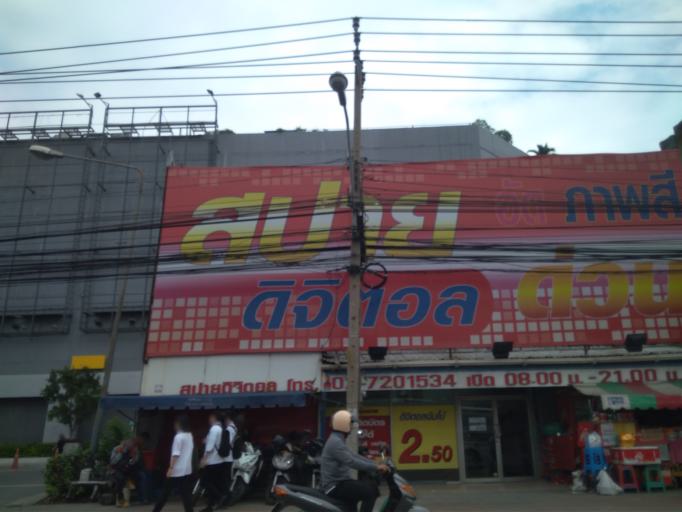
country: TH
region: Bangkok
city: Bang Na
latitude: 13.6923
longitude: 100.6473
